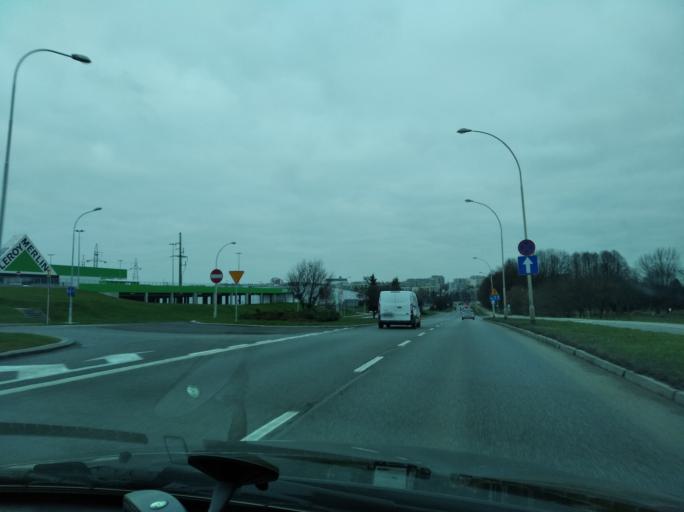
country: PL
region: Subcarpathian Voivodeship
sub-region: Rzeszow
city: Rzeszow
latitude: 50.0358
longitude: 21.9770
